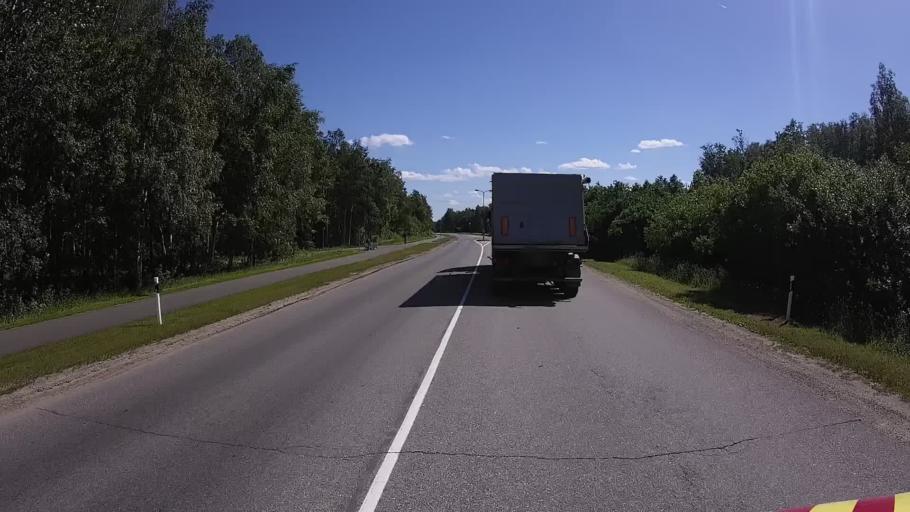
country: EE
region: Ida-Virumaa
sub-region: Kohtla-Jaerve linn
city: Kohtla-Jarve
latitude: 59.4154
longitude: 27.2755
